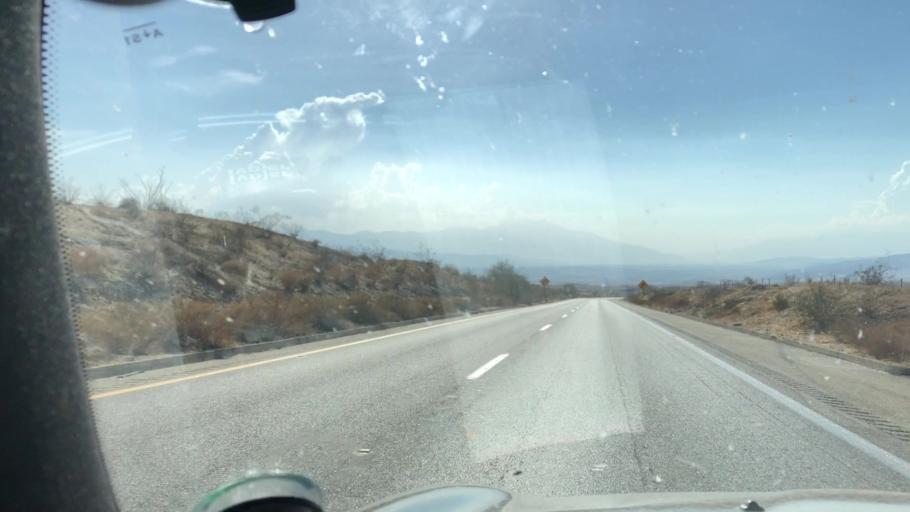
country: US
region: California
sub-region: Riverside County
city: Thermal
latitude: 33.6916
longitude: -116.0464
